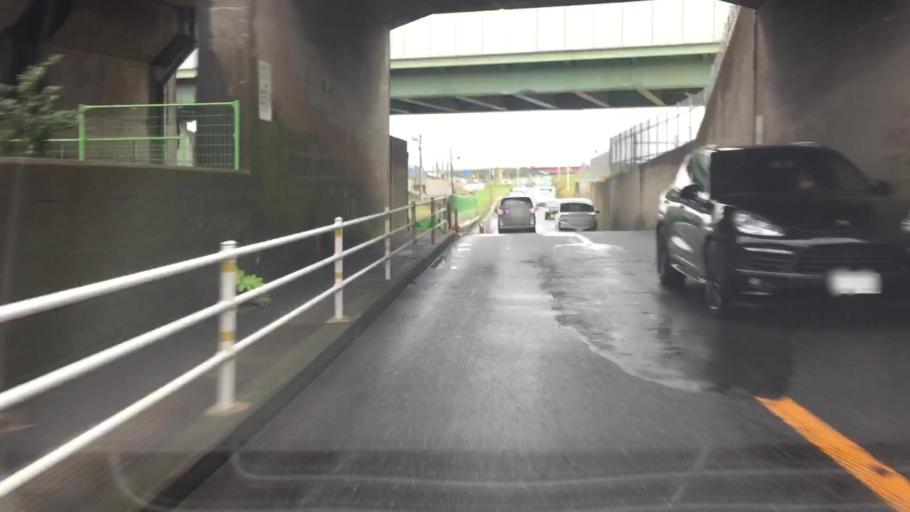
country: JP
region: Ibaraki
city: Toride
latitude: 35.8847
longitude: 140.0561
